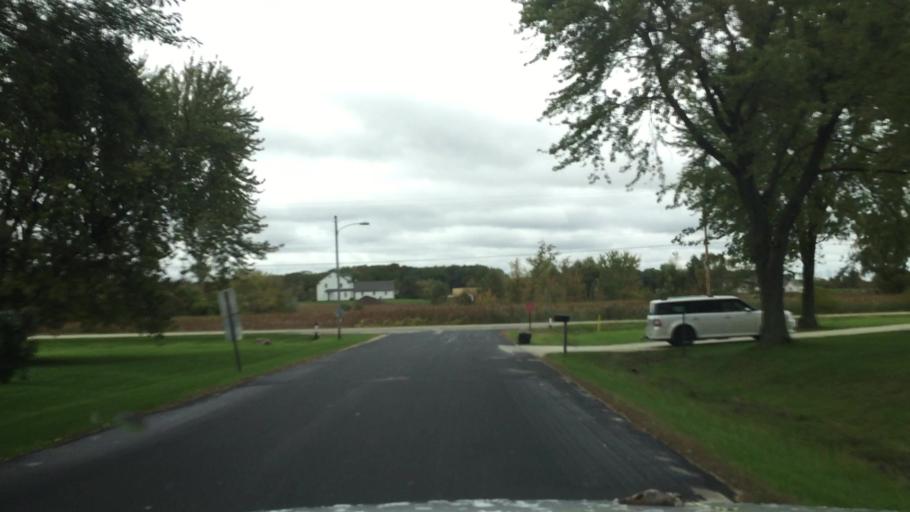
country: US
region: Wisconsin
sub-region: Racine County
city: Waterford
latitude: 42.7631
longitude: -88.1848
